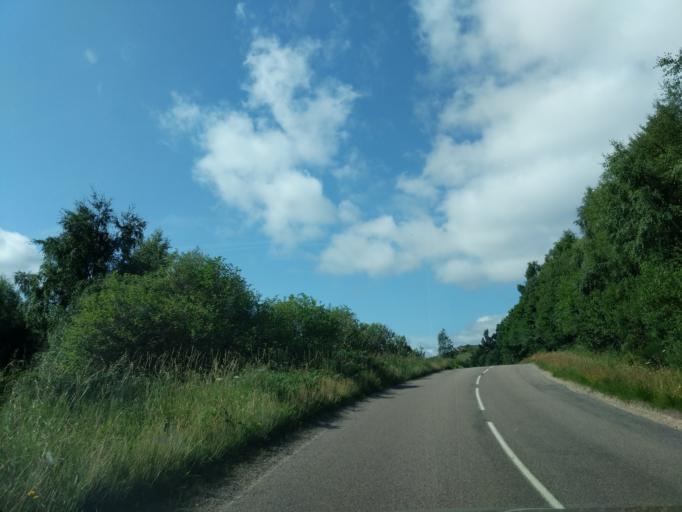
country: GB
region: Scotland
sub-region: Moray
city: Dufftown
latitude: 57.4156
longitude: -3.1646
